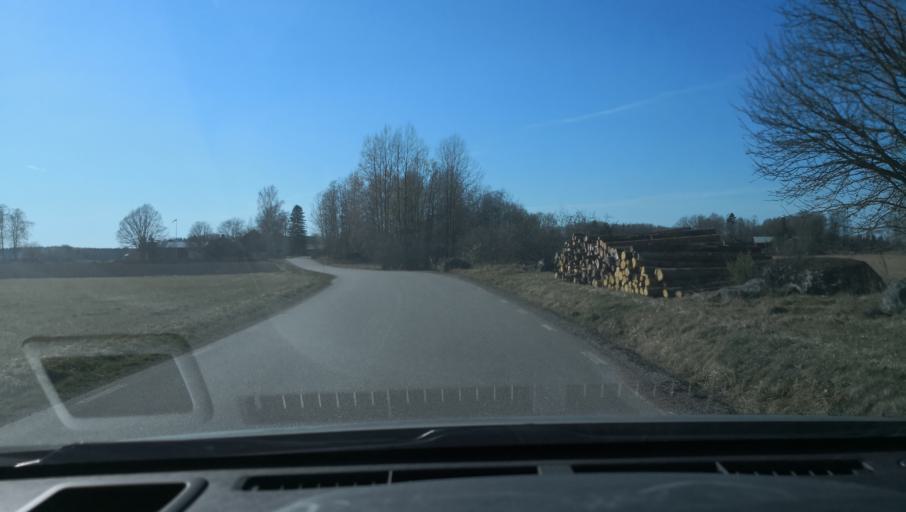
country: SE
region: Vaestmanland
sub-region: Sala Kommun
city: Sala
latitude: 60.0850
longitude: 16.5297
